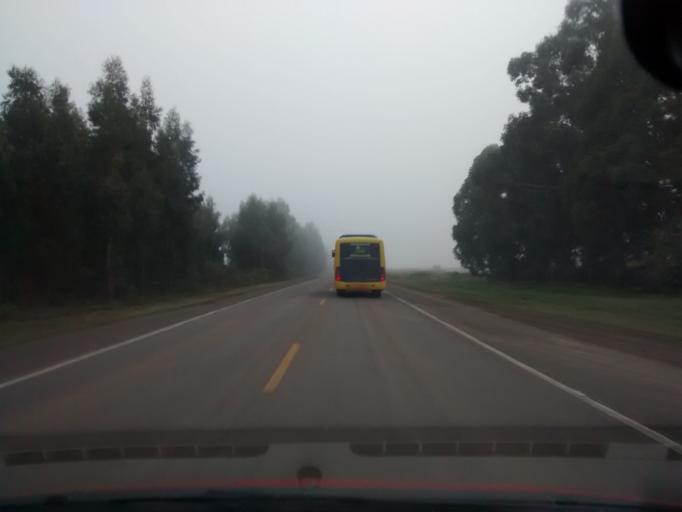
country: BR
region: Rio Grande do Sul
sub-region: Vacaria
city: Vacaria
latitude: -28.4261
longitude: -50.8679
